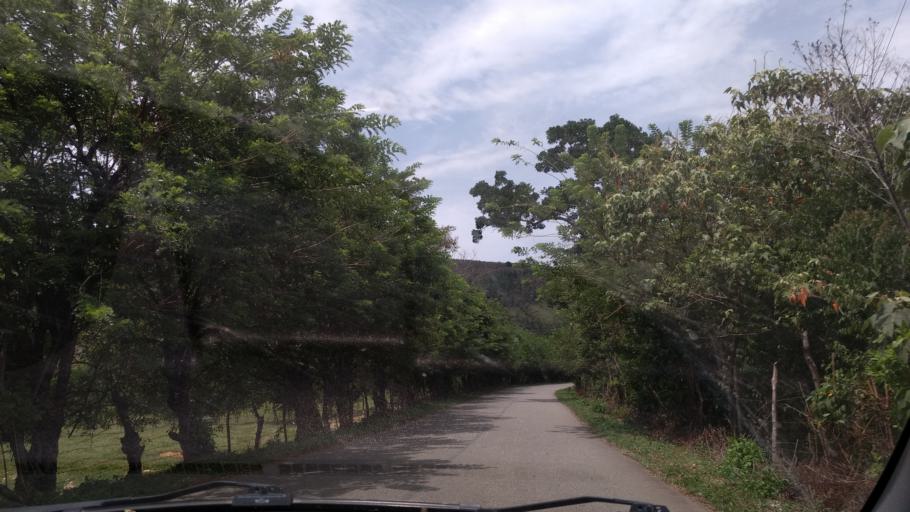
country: CO
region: Cauca
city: Buenos Aires
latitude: 3.0738
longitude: -76.6530
